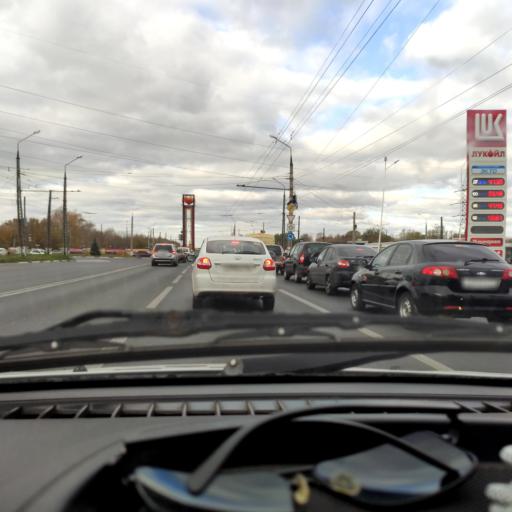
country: RU
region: Samara
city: Tol'yatti
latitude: 53.5505
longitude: 49.3200
